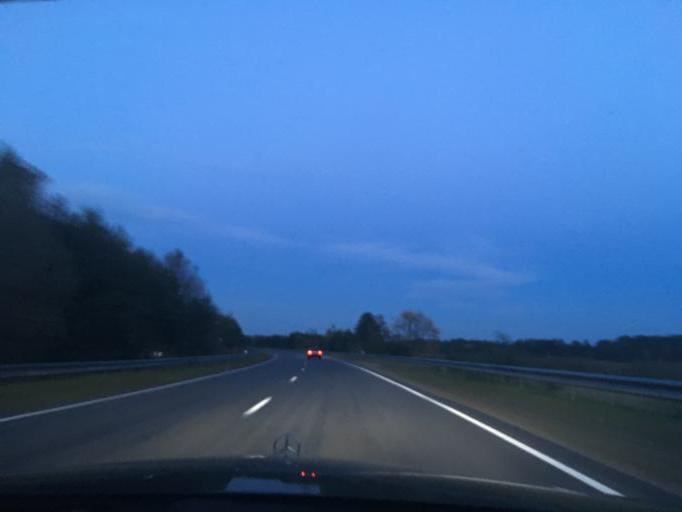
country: PL
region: Lublin Voivodeship
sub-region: Powiat bialski
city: Slawatycze
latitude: 51.7591
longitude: 23.6284
